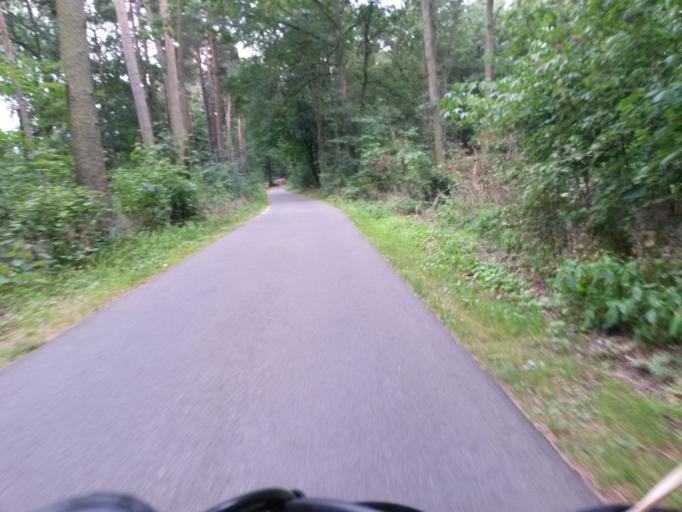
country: DE
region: Brandenburg
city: Angermunde
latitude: 53.0573
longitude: 13.9382
